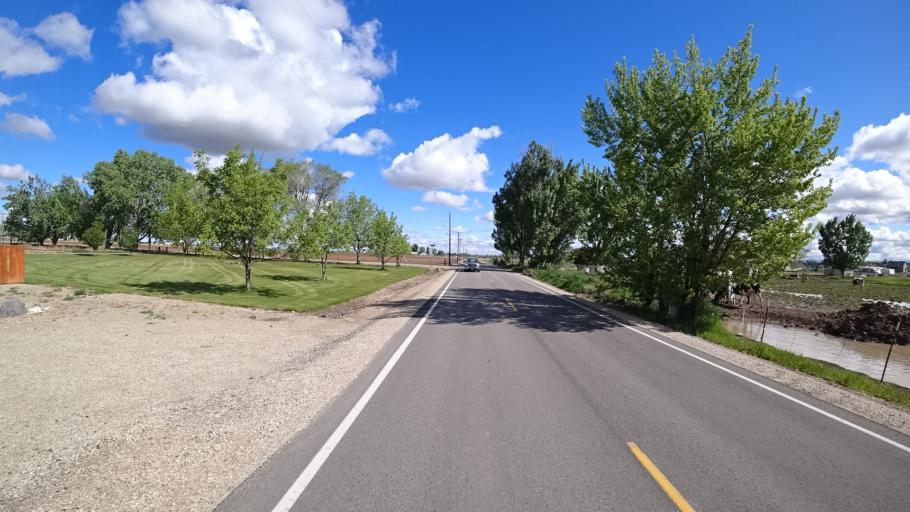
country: US
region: Idaho
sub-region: Ada County
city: Kuna
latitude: 43.5023
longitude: -116.4537
